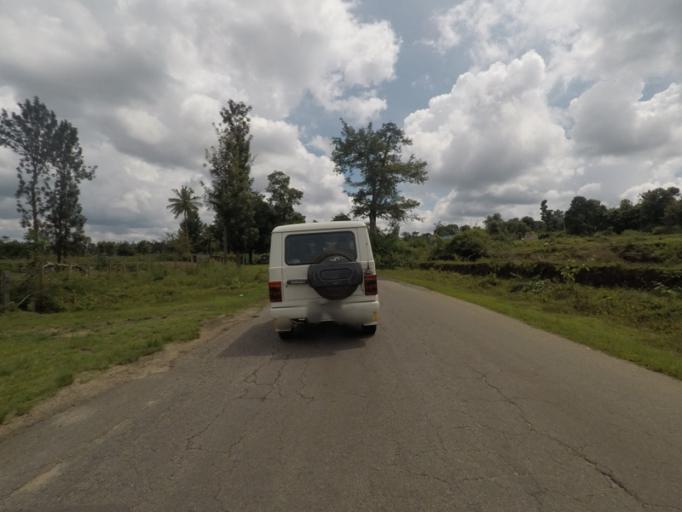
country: IN
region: Karnataka
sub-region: Kodagu
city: Kushalnagar
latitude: 12.4289
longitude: 75.9204
